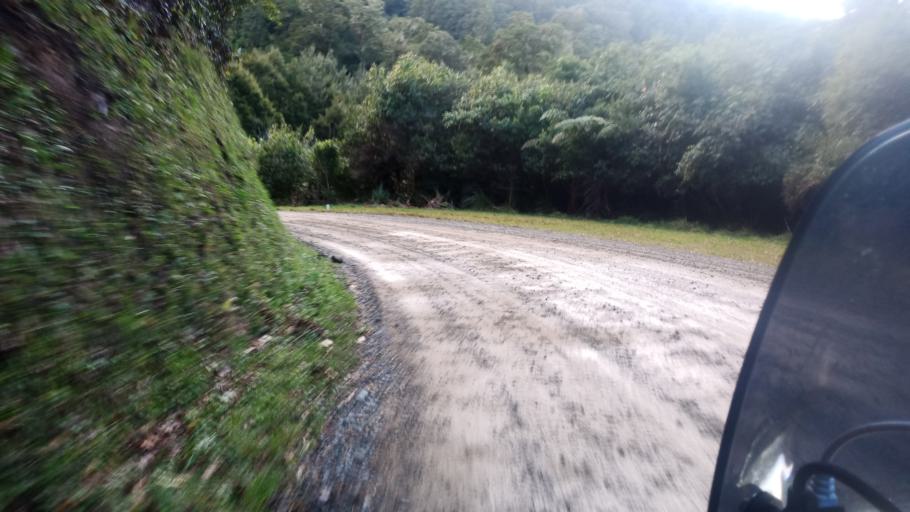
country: NZ
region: Hawke's Bay
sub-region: Wairoa District
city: Wairoa
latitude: -38.7448
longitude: 177.1159
